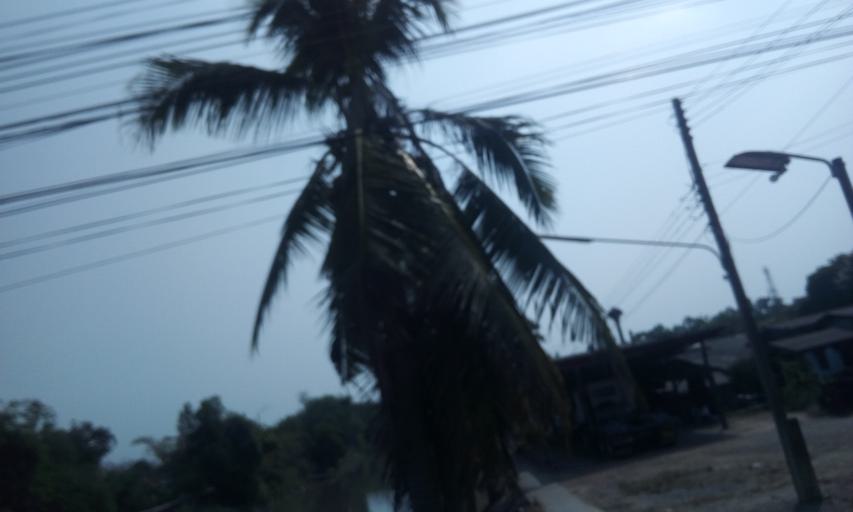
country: TH
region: Pathum Thani
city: Ban Lam Luk Ka
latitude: 13.9716
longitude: 100.7488
